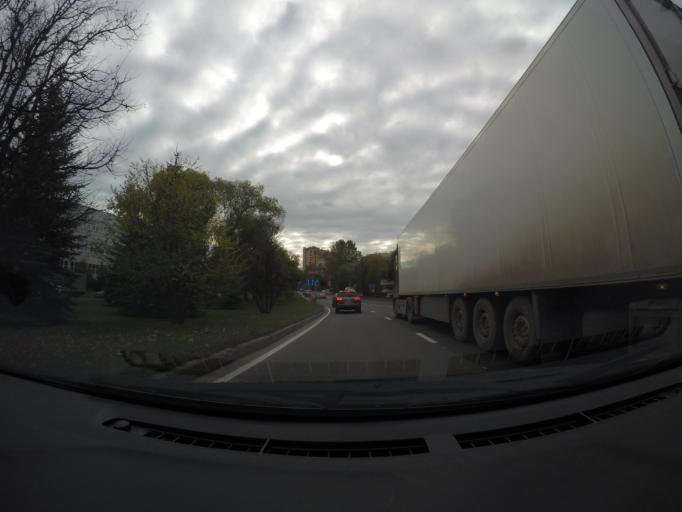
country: RU
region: Moskovskaya
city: Mytishchi
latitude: 55.9281
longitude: 37.7526
